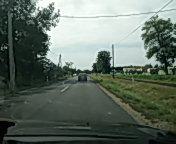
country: HU
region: Hajdu-Bihar
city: Debrecen
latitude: 47.5313
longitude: 21.7027
